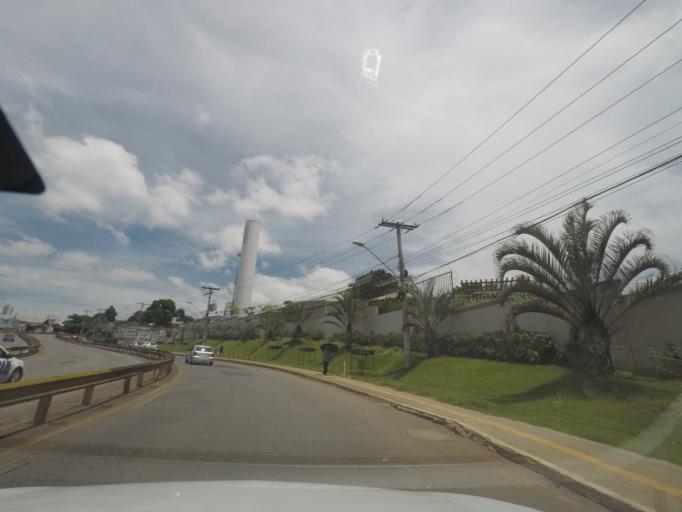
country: BR
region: Goias
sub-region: Goiania
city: Goiania
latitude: -16.6685
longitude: -49.2230
